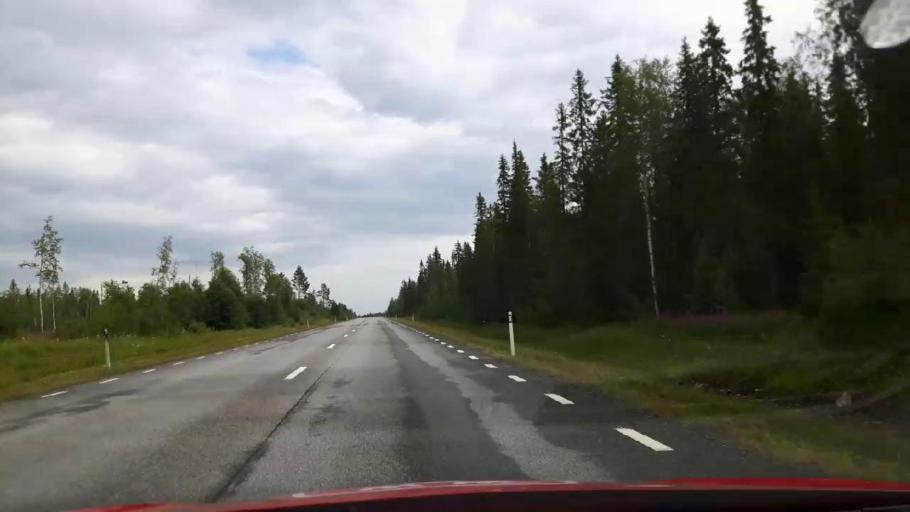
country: SE
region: Jaemtland
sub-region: Stroemsunds Kommun
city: Stroemsund
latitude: 63.6992
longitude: 15.4372
